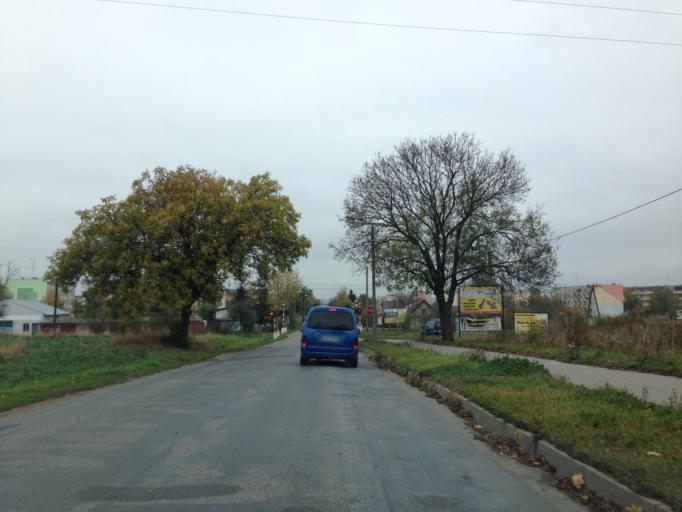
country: PL
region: Kujawsko-Pomorskie
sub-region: Powiat brodnicki
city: Brodnica
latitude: 53.2411
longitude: 19.4114
